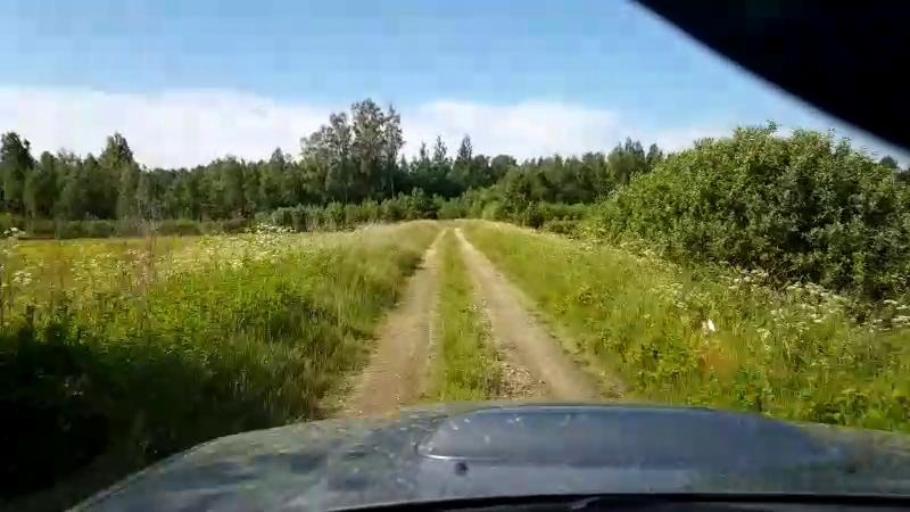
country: EE
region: Paernumaa
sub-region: Sindi linn
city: Sindi
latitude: 58.5045
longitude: 24.6405
